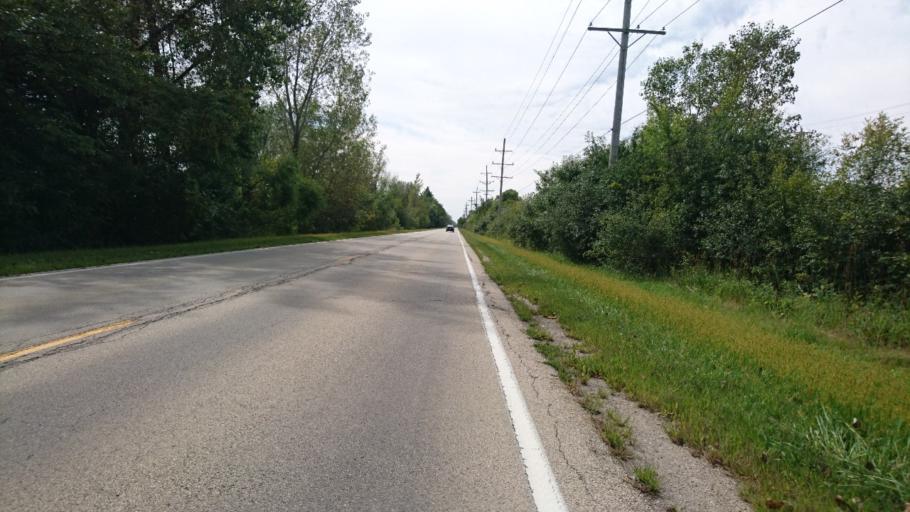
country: US
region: Illinois
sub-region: Will County
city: Braidwood
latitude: 41.2761
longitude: -88.1964
